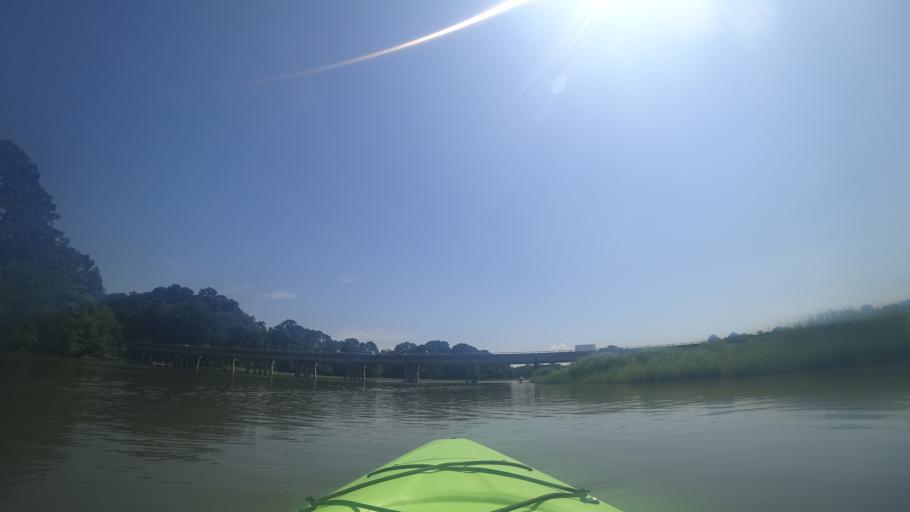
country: US
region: Virginia
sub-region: Isle of Wight County
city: Smithfield
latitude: 36.9662
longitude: -76.6130
